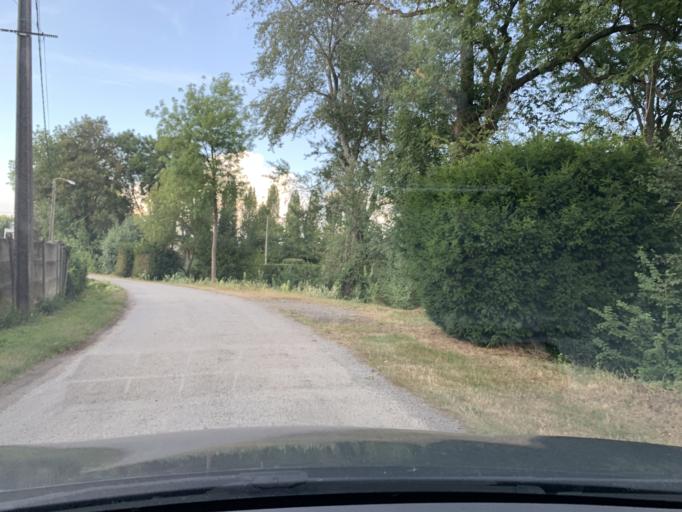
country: FR
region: Nord-Pas-de-Calais
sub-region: Departement du Nord
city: Cambrai
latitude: 50.1705
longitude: 3.2218
